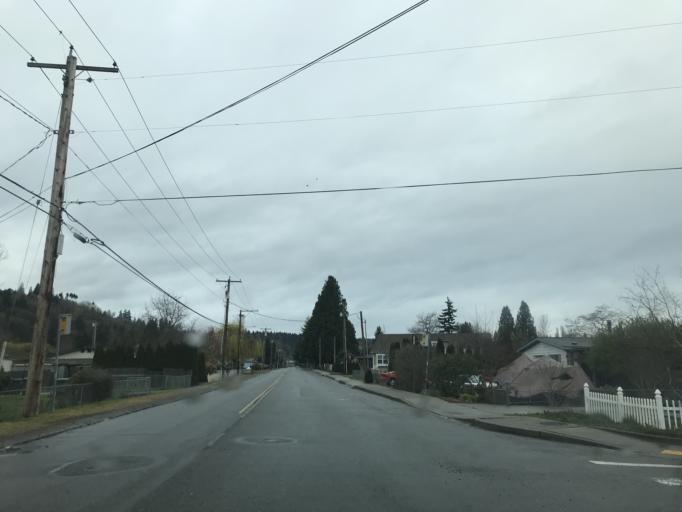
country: US
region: Washington
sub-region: King County
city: Algona
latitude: 47.2807
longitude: -122.2520
